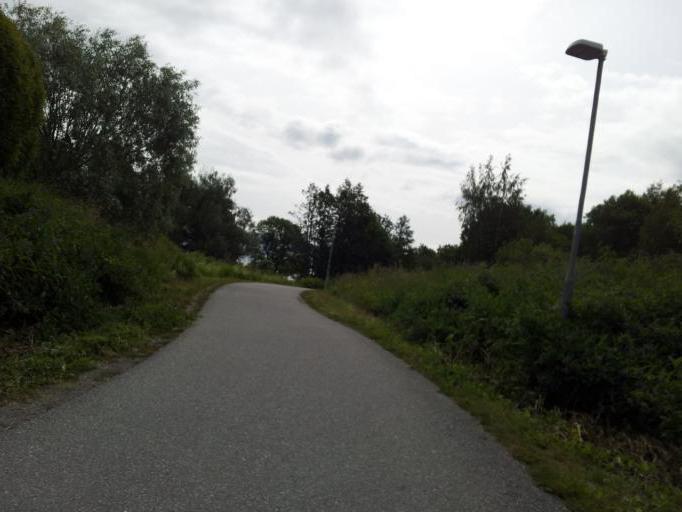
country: SE
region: Uppsala
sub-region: Uppsala Kommun
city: Gamla Uppsala
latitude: 59.8754
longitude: 17.6068
